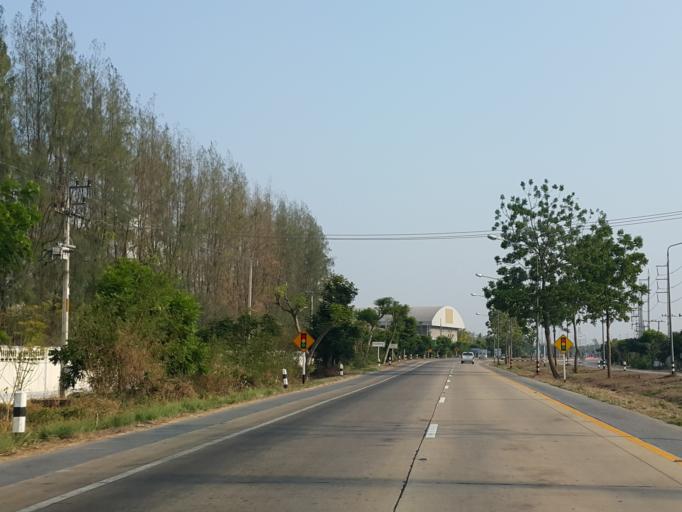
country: TH
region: Chai Nat
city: Hankha
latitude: 14.9492
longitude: 100.0817
